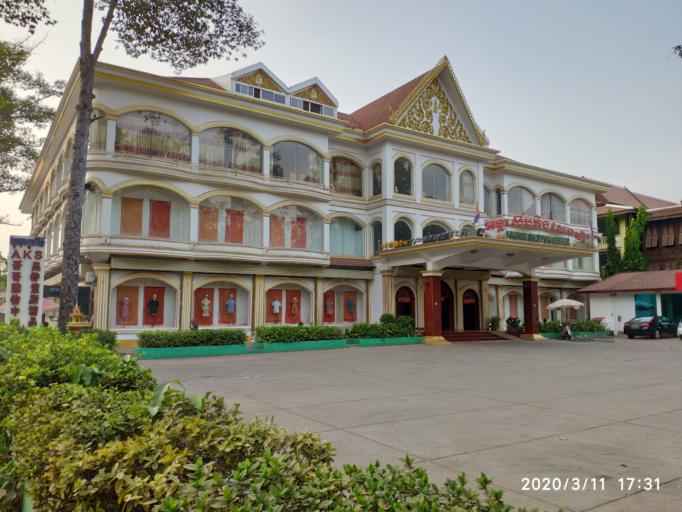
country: KH
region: Siem Reap
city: Siem Reap
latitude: 13.3628
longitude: 103.8577
